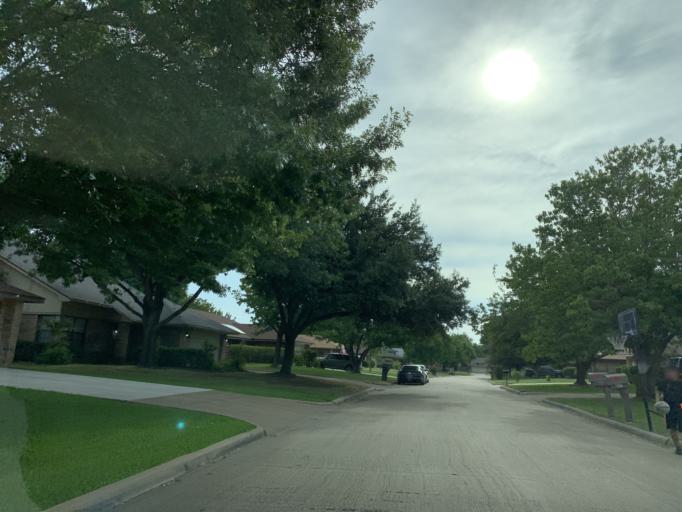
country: US
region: Texas
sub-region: Dallas County
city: Grand Prairie
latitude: 32.6639
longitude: -97.0456
